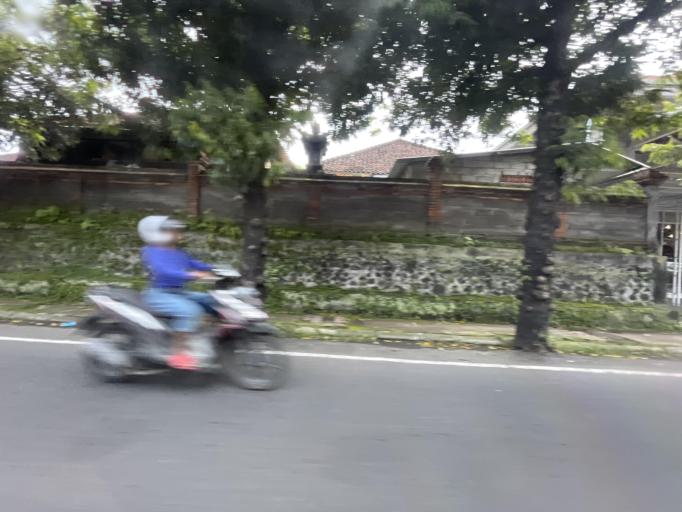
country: ID
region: Bali
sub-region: Kabupaten Gianyar
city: Ubud
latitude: -8.5237
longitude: 115.2709
